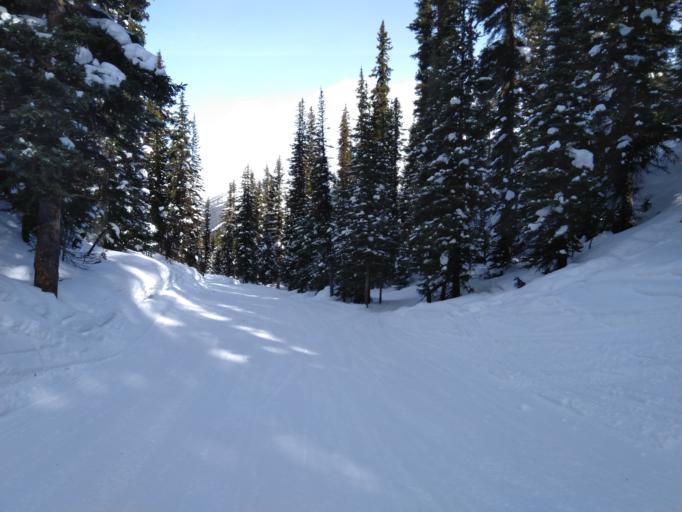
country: CA
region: Alberta
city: Banff
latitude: 51.0925
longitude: -115.7702
